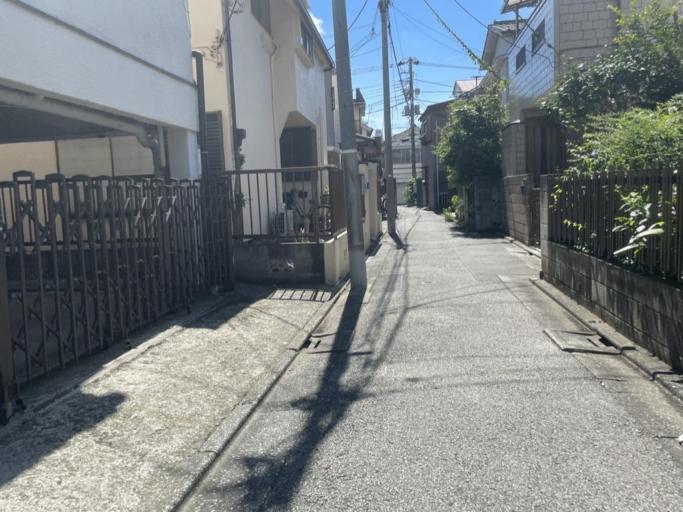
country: JP
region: Chiba
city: Matsudo
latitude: 35.7365
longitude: 139.8495
